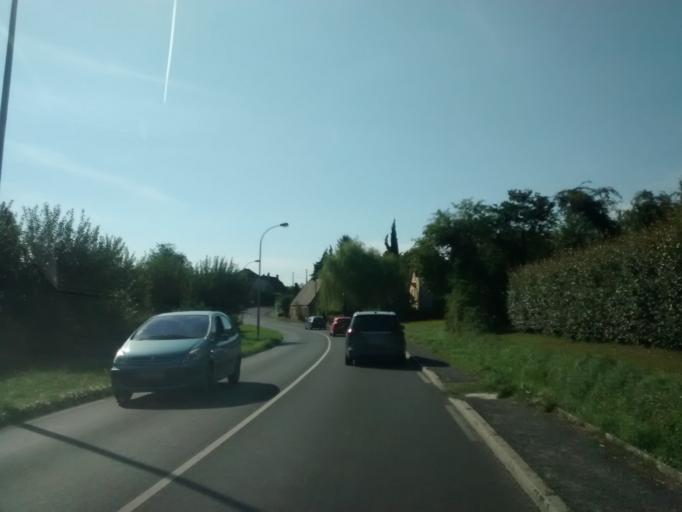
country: FR
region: Aquitaine
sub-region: Departement de la Dordogne
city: Sarlat-la-Caneda
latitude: 44.9048
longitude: 1.2081
